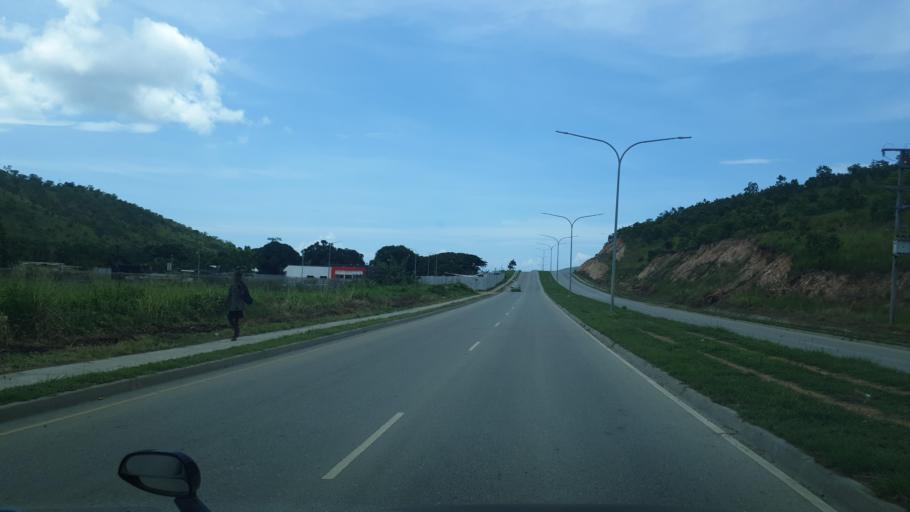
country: PG
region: National Capital
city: Port Moresby
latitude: -9.4321
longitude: 147.1409
